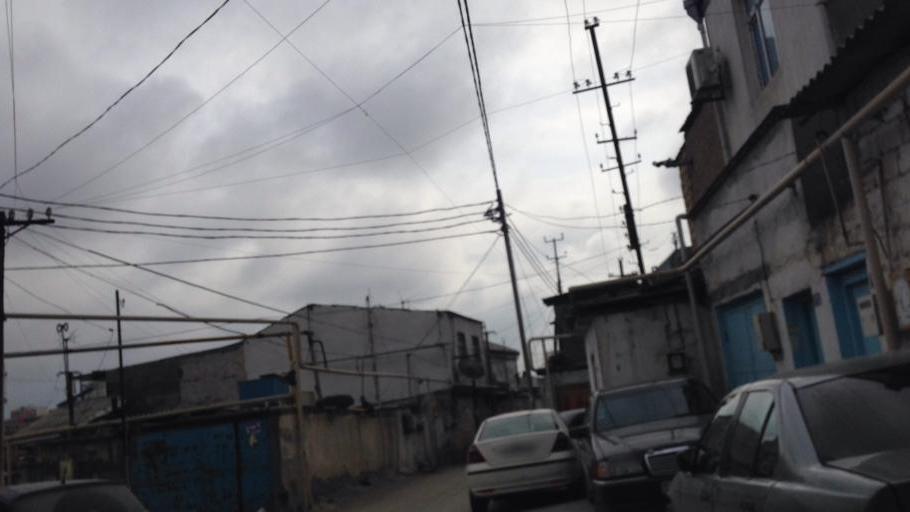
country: AZ
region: Baki
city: Bilajari
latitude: 40.4058
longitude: 49.8261
